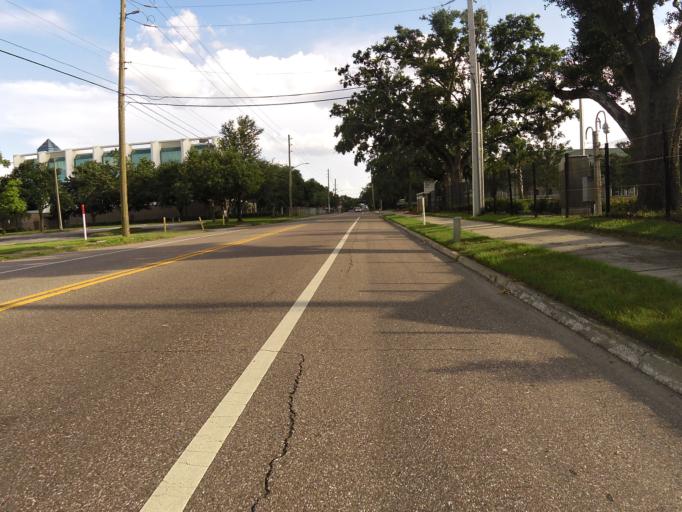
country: US
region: Florida
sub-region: Duval County
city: Jacksonville
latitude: 30.3367
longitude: -81.6640
